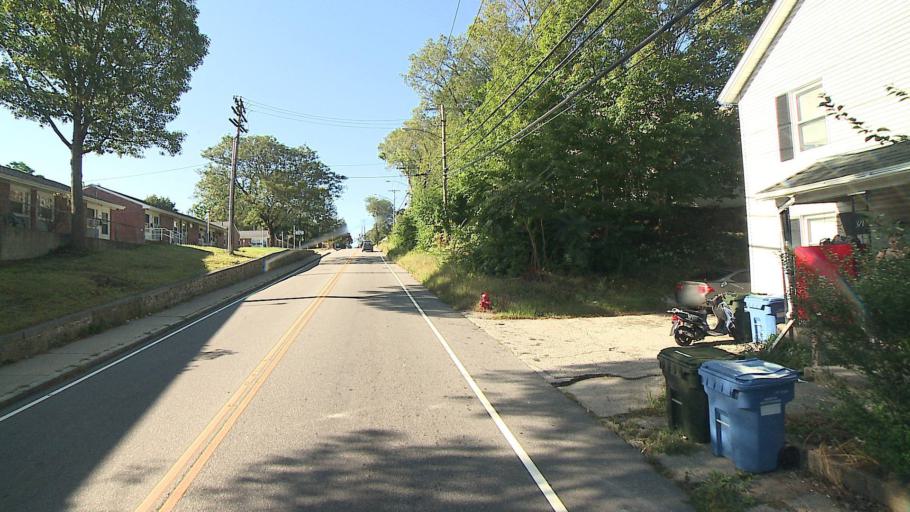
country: US
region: Connecticut
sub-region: New London County
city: Norwich
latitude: 41.5108
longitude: -72.0751
